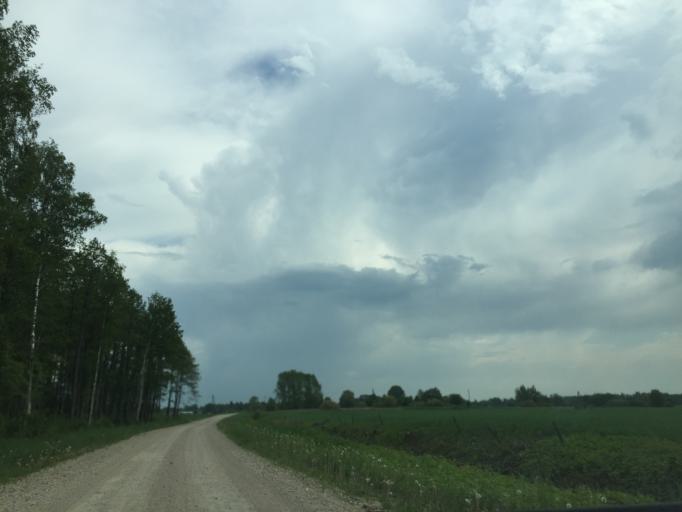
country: LV
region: Livani
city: Livani
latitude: 56.5530
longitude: 26.2273
